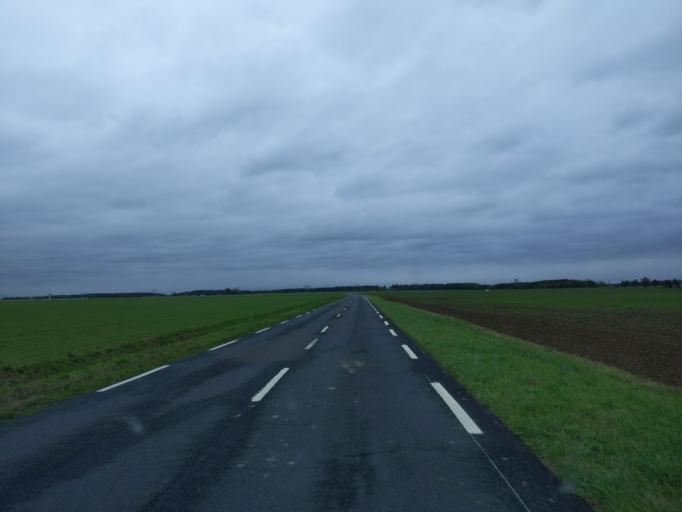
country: FR
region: Ile-de-France
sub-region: Departement des Yvelines
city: Cernay-la-Ville
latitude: 48.6605
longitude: 1.9876
